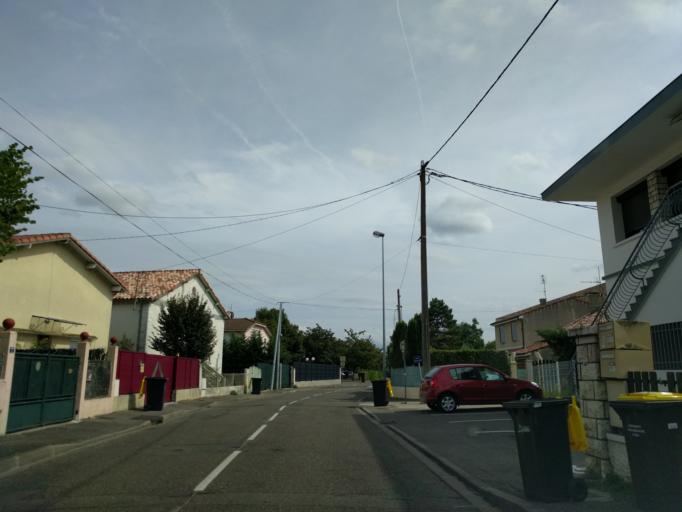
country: FR
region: Aquitaine
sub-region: Departement du Lot-et-Garonne
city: Agen
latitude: 44.1918
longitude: 0.6342
